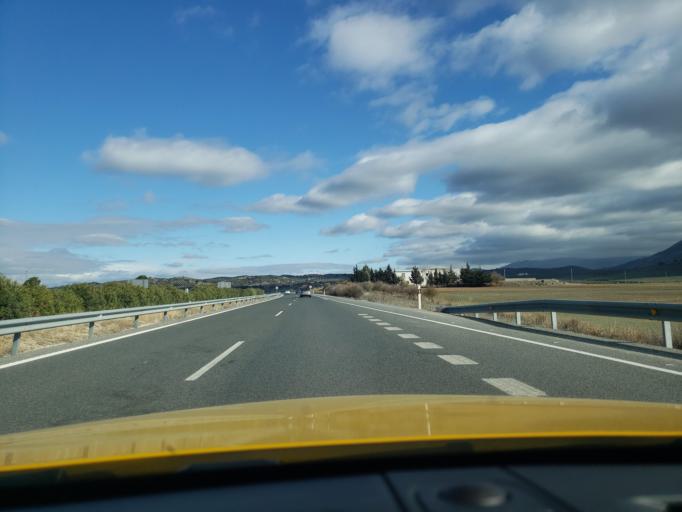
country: ES
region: Andalusia
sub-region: Provincia de Malaga
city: Villanueva del Trabuco
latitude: 37.0697
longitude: -4.3253
